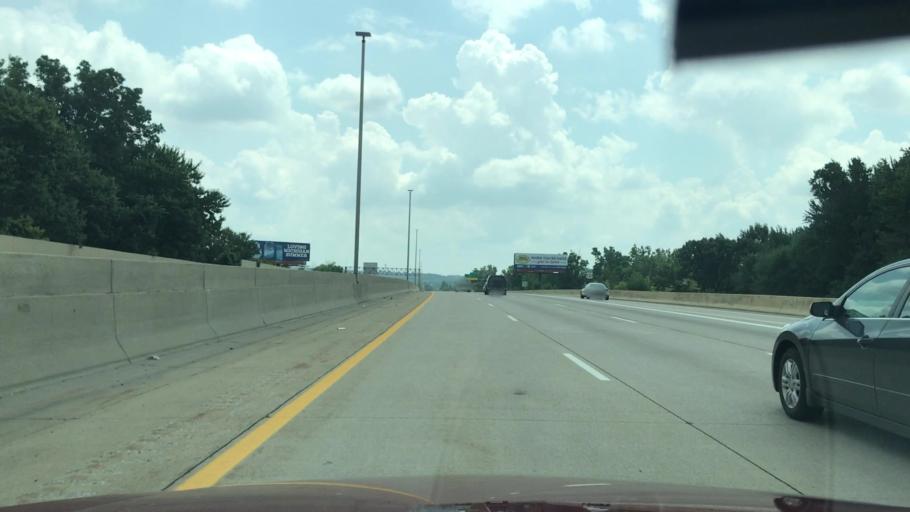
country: US
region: Michigan
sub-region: Kent County
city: Cutlerville
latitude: 42.8338
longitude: -85.6760
